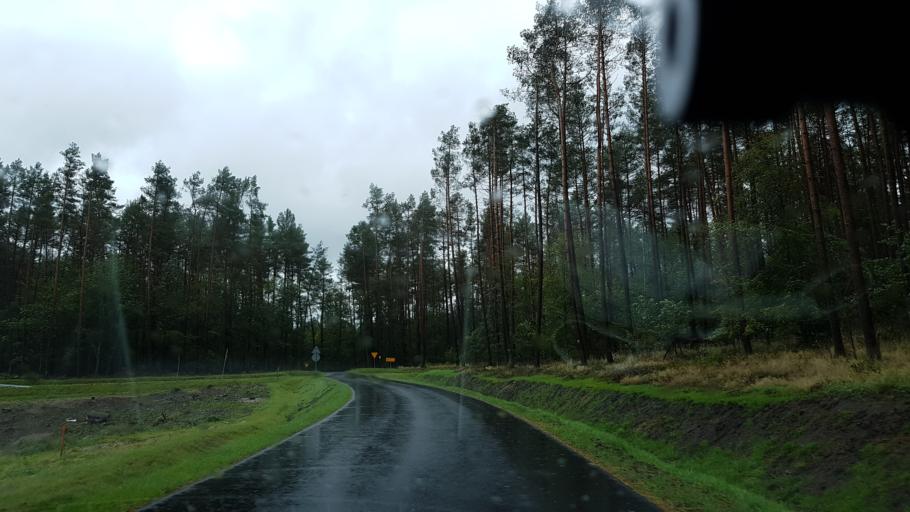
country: PL
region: West Pomeranian Voivodeship
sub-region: Powiat goleniowski
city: Przybiernow
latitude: 53.7386
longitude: 14.7716
